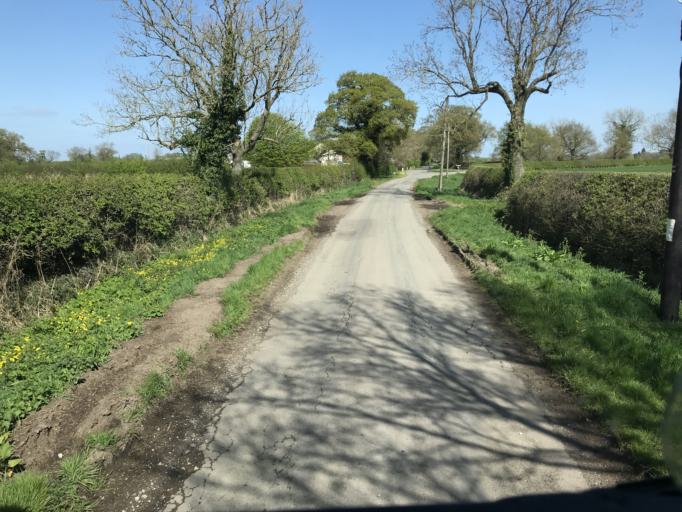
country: GB
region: England
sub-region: Cheshire East
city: Nantwich
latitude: 53.1045
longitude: -2.5355
